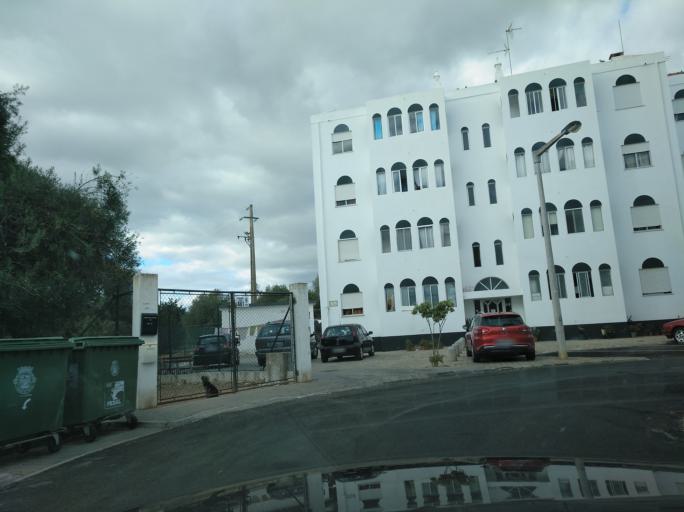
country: PT
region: Faro
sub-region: Tavira
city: Luz
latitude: 37.0931
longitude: -7.7055
